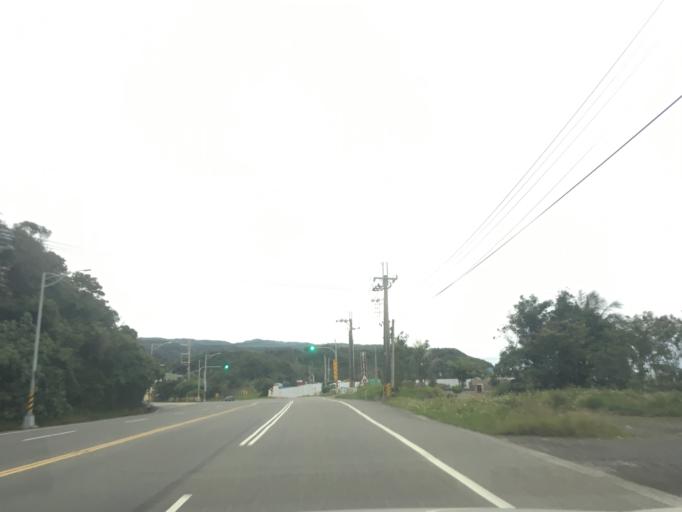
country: TW
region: Taiwan
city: Hengchun
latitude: 22.3358
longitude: 120.8942
